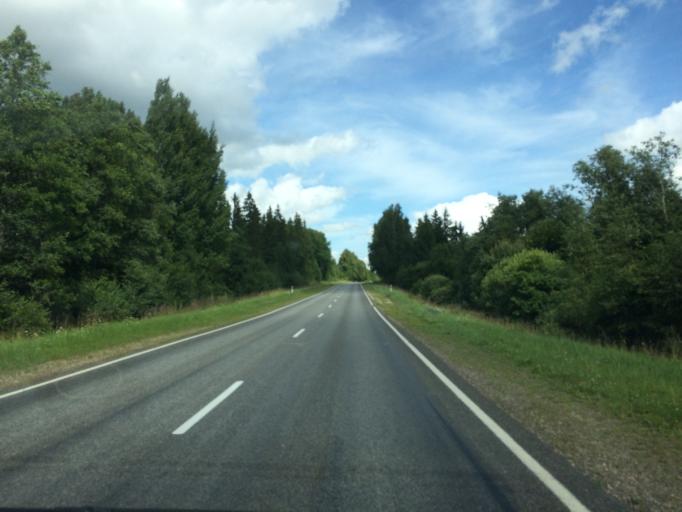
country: LV
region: Rezekne
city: Rezekne
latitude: 56.6261
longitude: 27.4603
